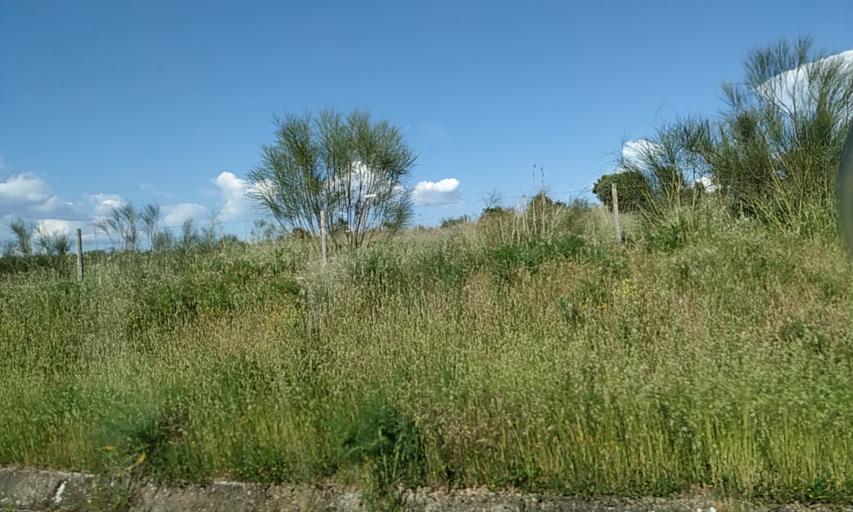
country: PT
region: Portalegre
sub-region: Portalegre
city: Urra
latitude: 39.0814
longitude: -7.4371
